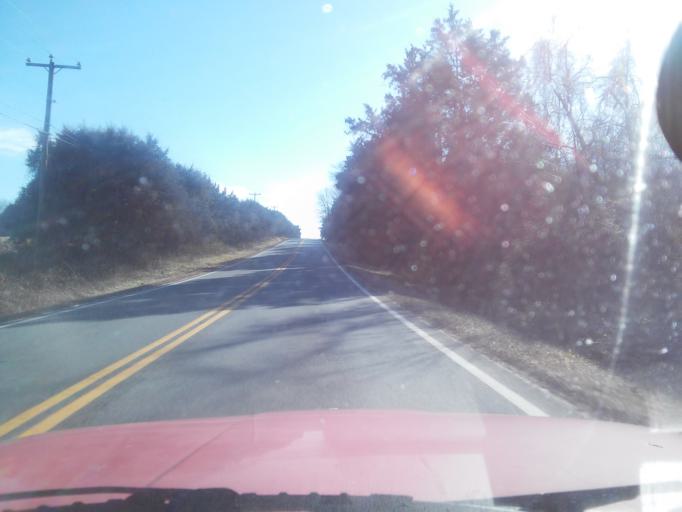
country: US
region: Virginia
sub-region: Orange County
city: Gordonsville
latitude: 38.0594
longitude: -78.1881
